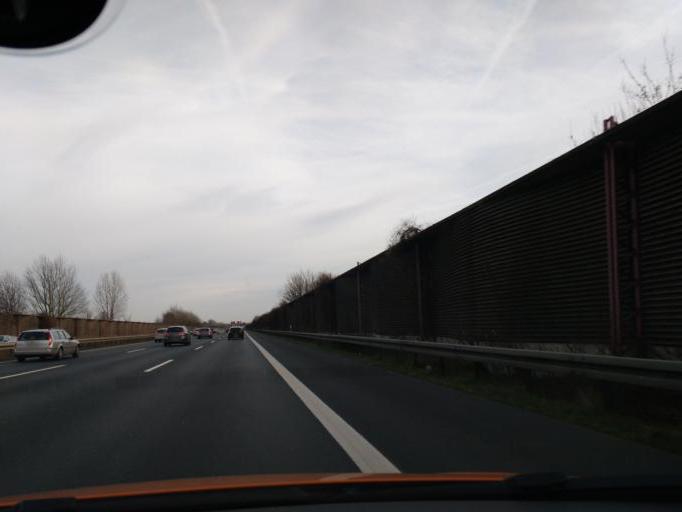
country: DE
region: Lower Saxony
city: Edemissen
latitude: 52.3382
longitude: 10.3168
